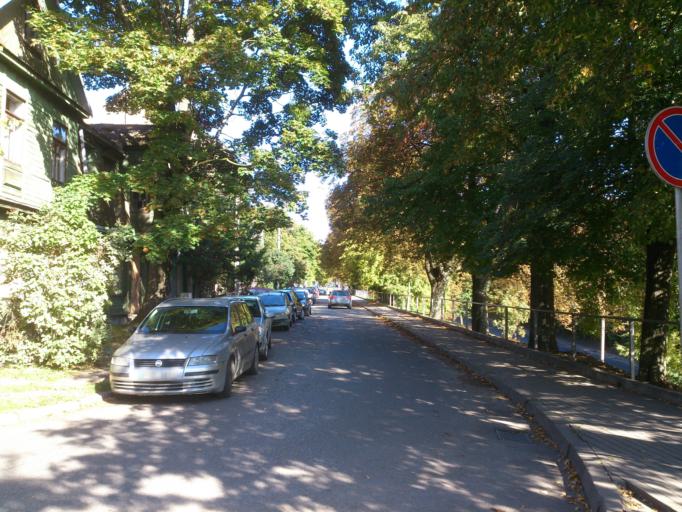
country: LT
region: Kauno apskritis
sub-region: Kaunas
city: Kaunas
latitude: 54.9021
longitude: 23.9095
